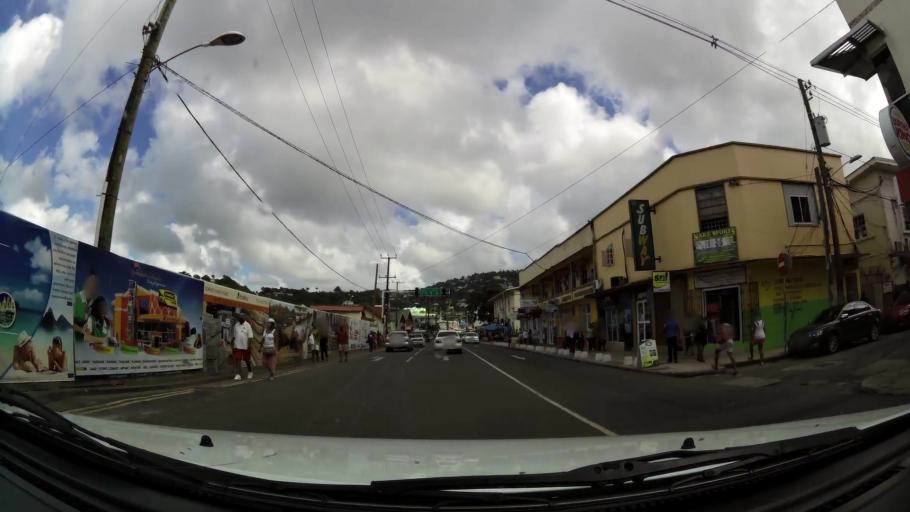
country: LC
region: Castries Quarter
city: Bisee
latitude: 14.0110
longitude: -60.9907
